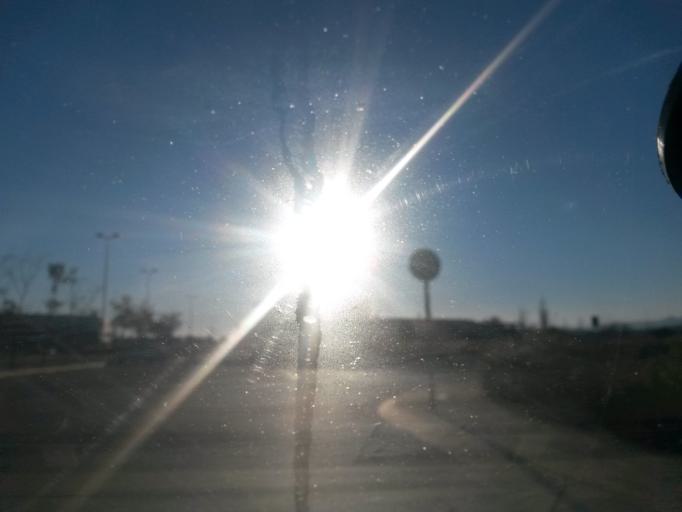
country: ES
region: Catalonia
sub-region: Provincia de Girona
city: Salt
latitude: 41.9589
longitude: 2.8015
